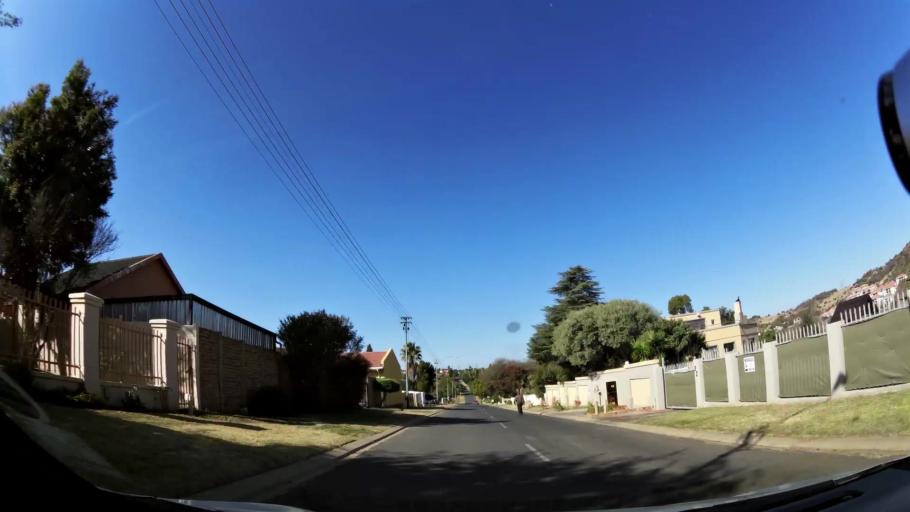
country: ZA
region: Gauteng
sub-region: City of Johannesburg Metropolitan Municipality
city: Johannesburg
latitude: -26.2744
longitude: 28.0209
